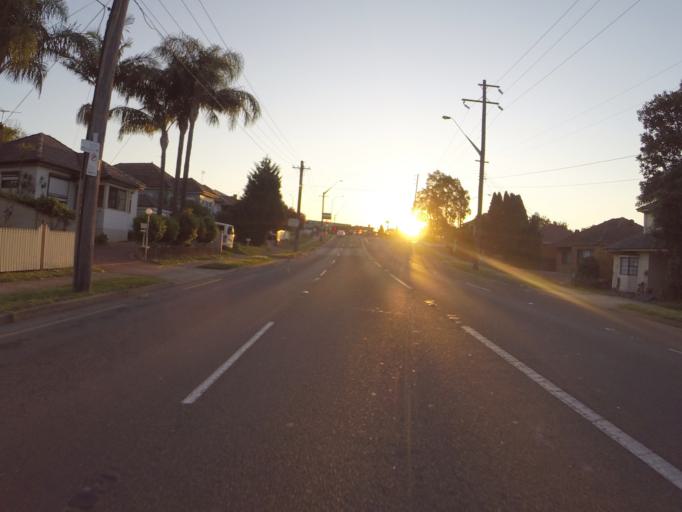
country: AU
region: New South Wales
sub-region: Hurstville
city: Penshurst
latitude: -33.9579
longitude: 151.0708
